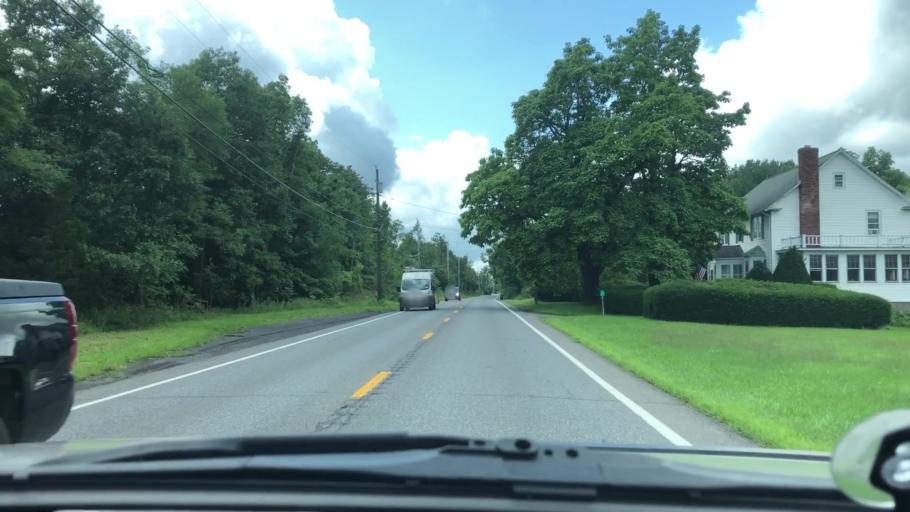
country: US
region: New York
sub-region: Greene County
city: Palenville
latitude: 42.1517
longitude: -74.0000
